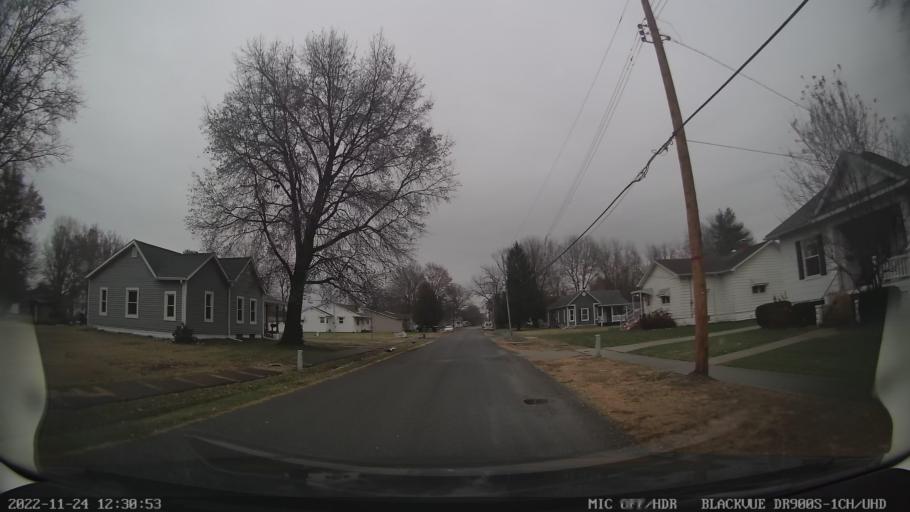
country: US
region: Illinois
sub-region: Macoupin County
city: Staunton
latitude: 39.0160
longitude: -89.7840
